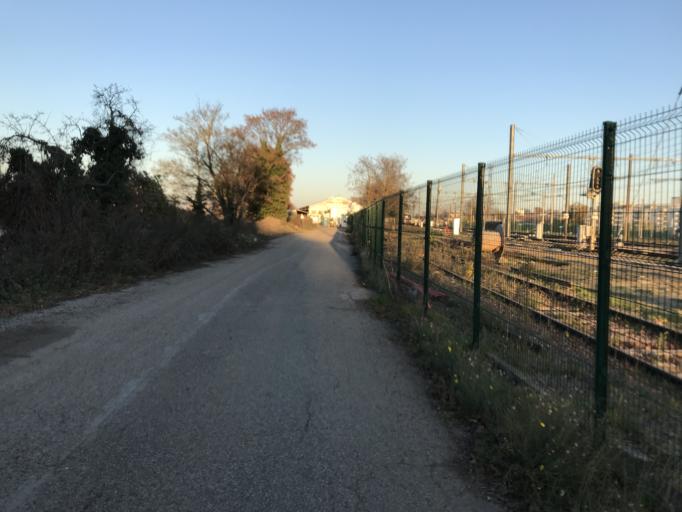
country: FR
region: Ile-de-France
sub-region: Departement de l'Essonne
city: Verrieres-le-Buisson
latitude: 48.7298
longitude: 2.2626
